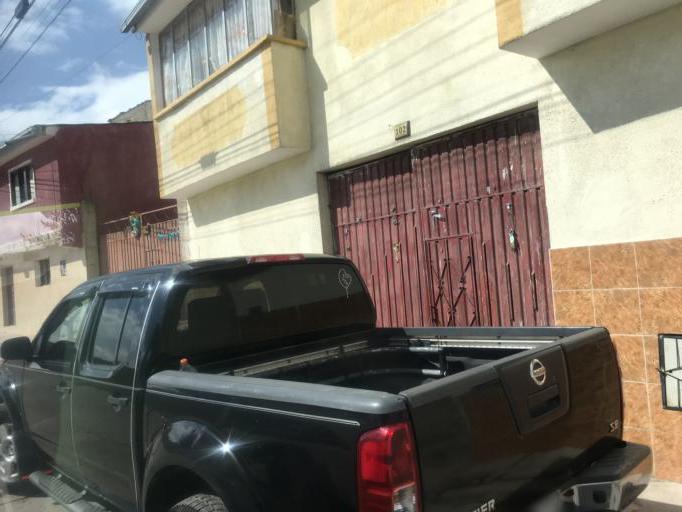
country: BO
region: Potosi
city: Potosi
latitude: -19.5998
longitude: -65.7437
